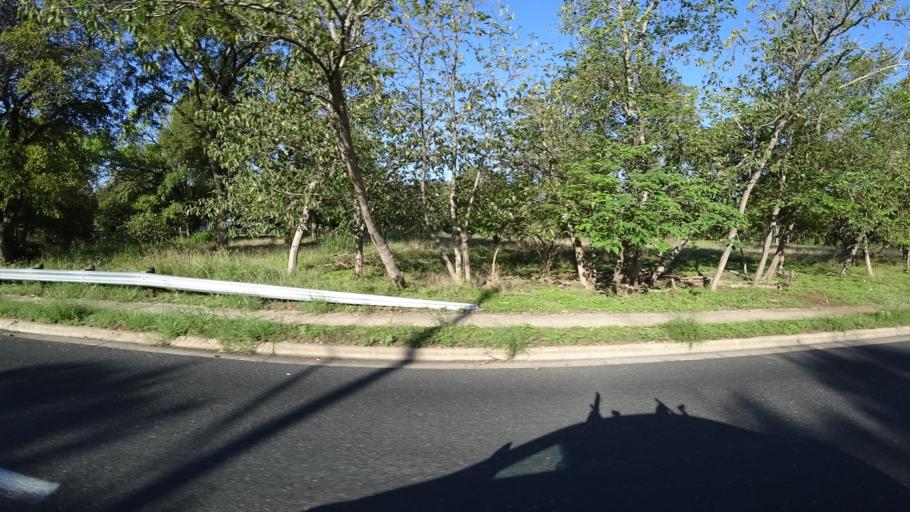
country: US
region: Texas
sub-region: Travis County
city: Rollingwood
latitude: 30.2204
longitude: -97.8069
